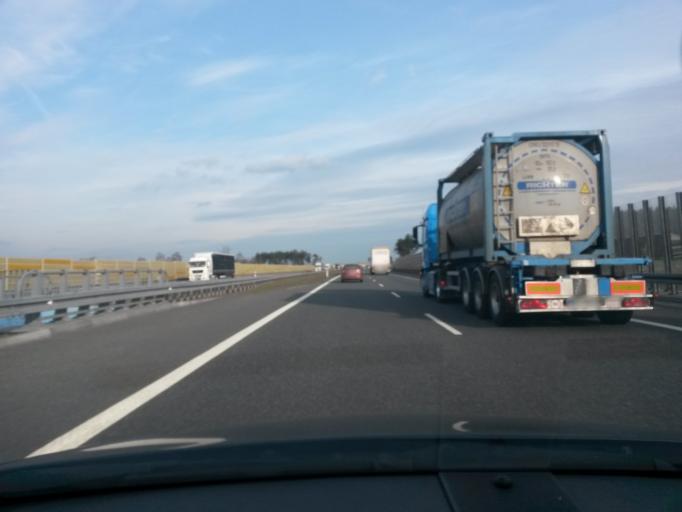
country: PL
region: Lodz Voivodeship
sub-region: Powiat zgierski
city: Ozorkow
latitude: 51.9344
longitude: 19.2701
